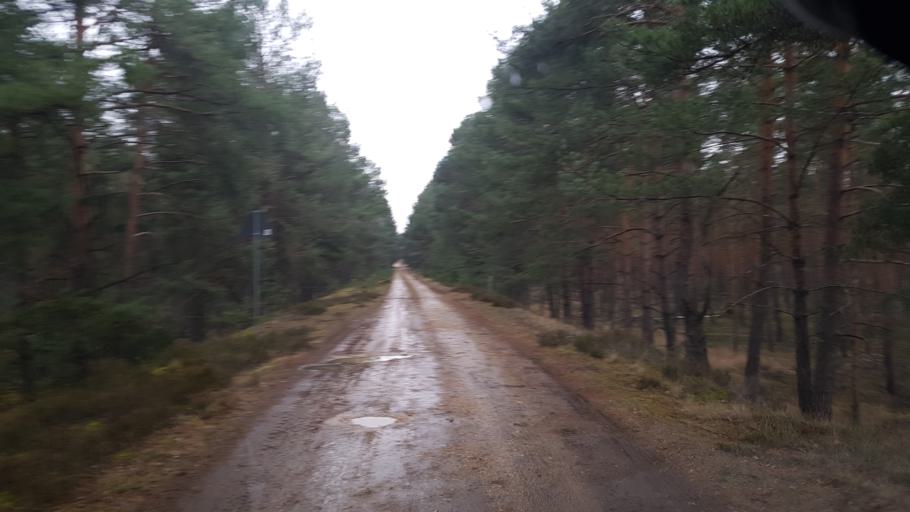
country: DE
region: Brandenburg
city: Crinitz
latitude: 51.6717
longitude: 13.8223
